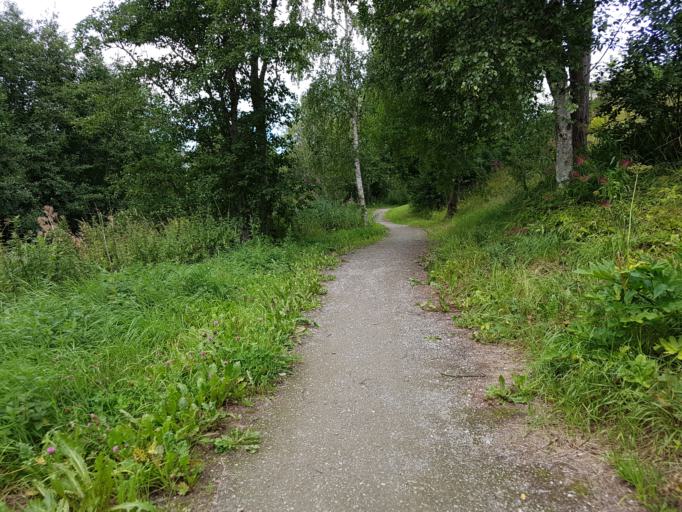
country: NO
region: Sor-Trondelag
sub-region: Trondheim
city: Trondheim
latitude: 63.4241
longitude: 10.4593
